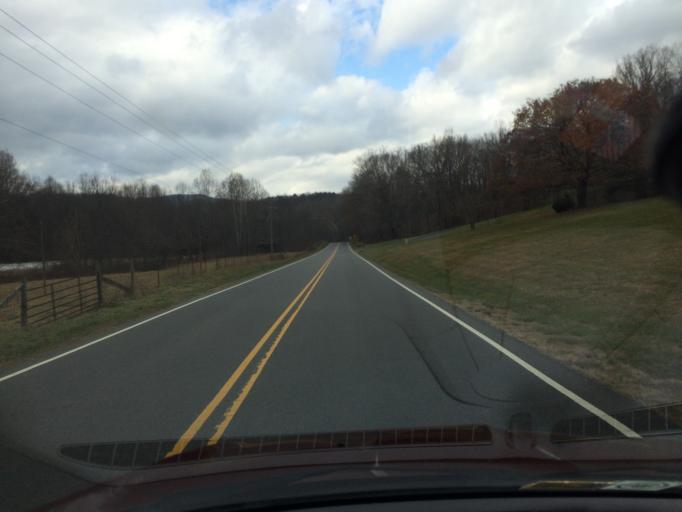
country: US
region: Virginia
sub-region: Patrick County
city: Stuart
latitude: 36.7484
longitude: -80.2653
